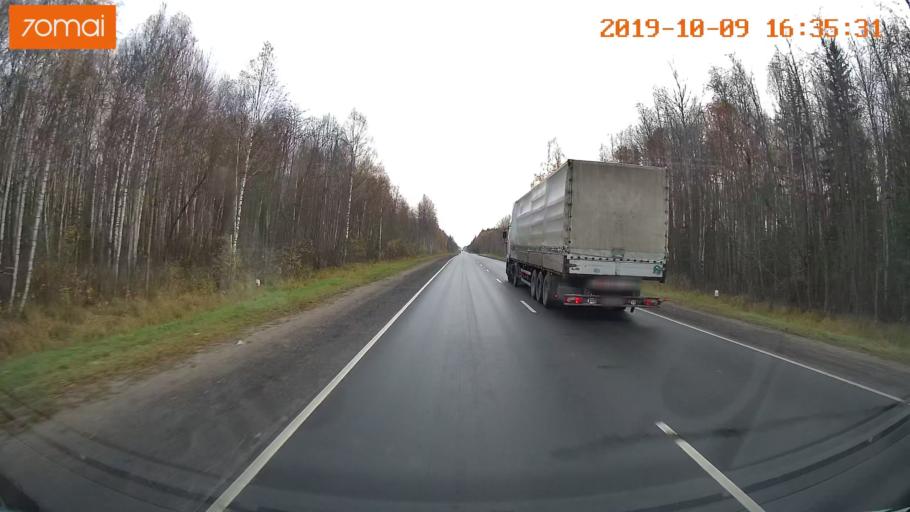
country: RU
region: Kostroma
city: Oktyabr'skiy
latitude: 57.5546
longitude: 41.0018
